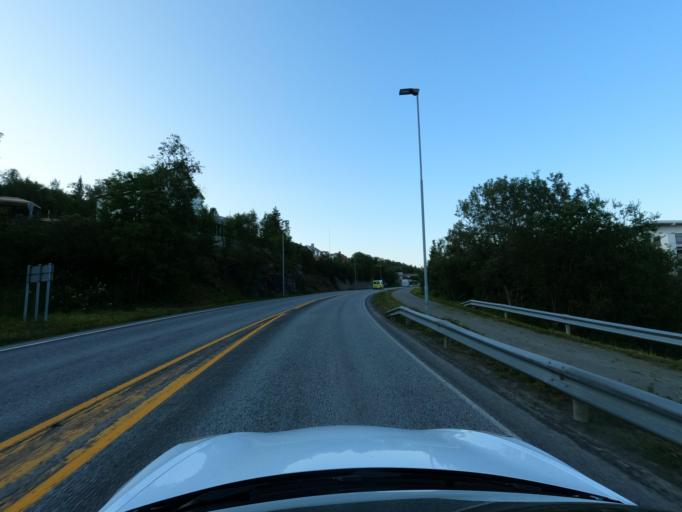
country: NO
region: Troms
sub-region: Harstad
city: Harstad
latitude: 68.7477
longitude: 16.5582
